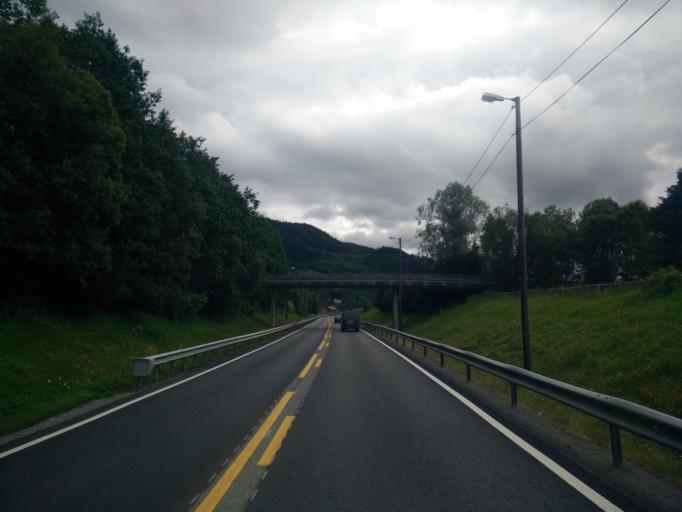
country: NO
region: Sor-Trondelag
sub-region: Orkdal
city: Orkanger
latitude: 63.2927
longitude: 9.8523
